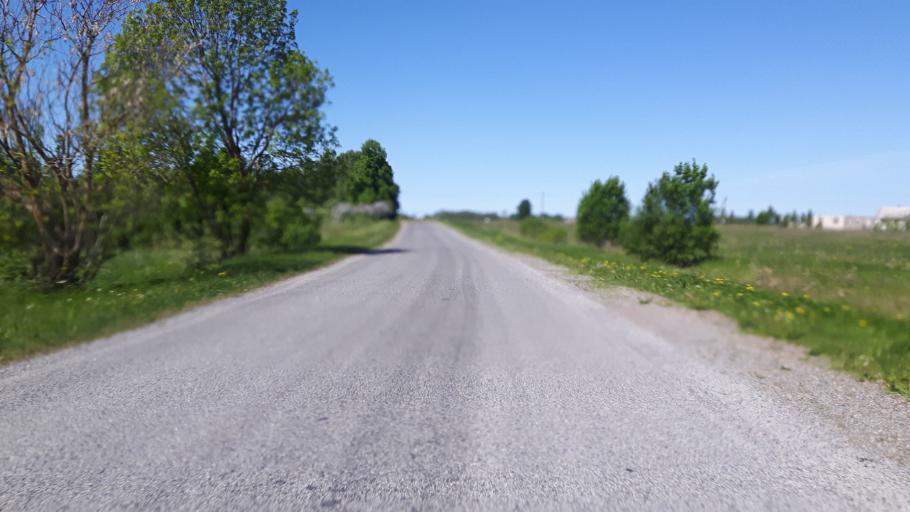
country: EE
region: Ida-Virumaa
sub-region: Sillamaee linn
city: Sillamae
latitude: 59.3804
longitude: 27.8284
